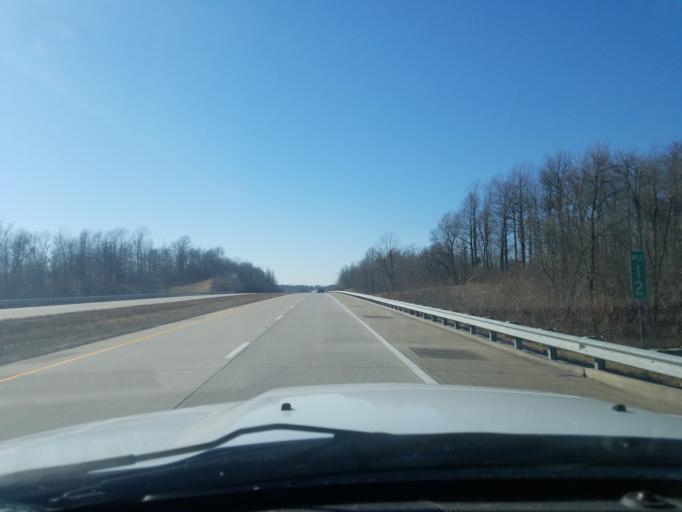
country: US
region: Indiana
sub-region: Warrick County
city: Newburgh
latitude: 37.7550
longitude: -87.3632
